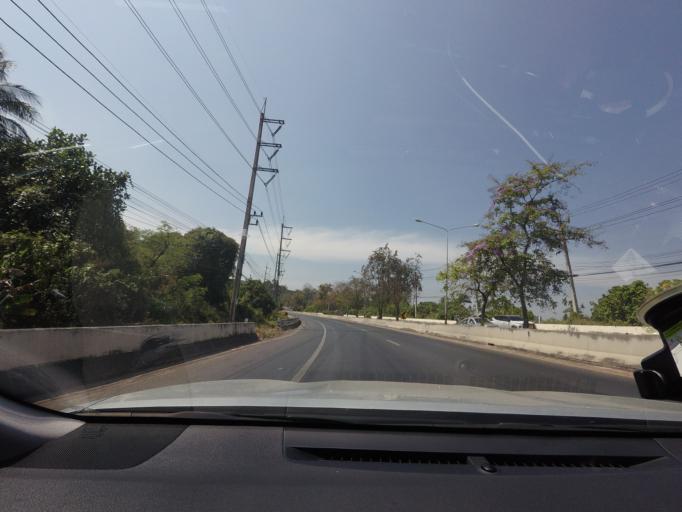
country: TH
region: Surat Thani
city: Kanchanadit
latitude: 9.1546
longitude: 99.4161
